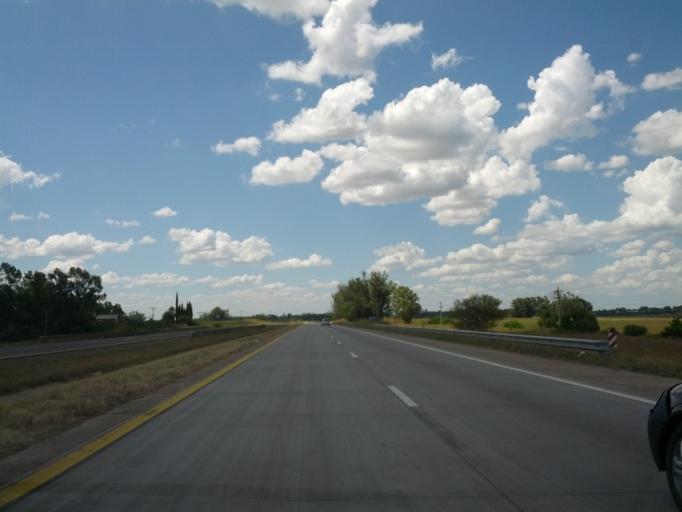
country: UY
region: Paysandu
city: San Felix
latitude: -32.3199
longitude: -58.2568
